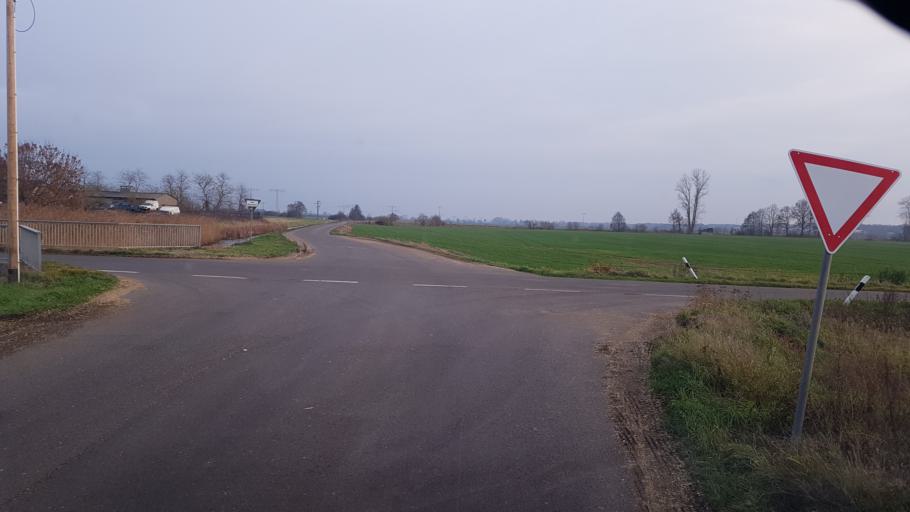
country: DE
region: Brandenburg
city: Wiesenau
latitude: 52.2369
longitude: 14.6011
